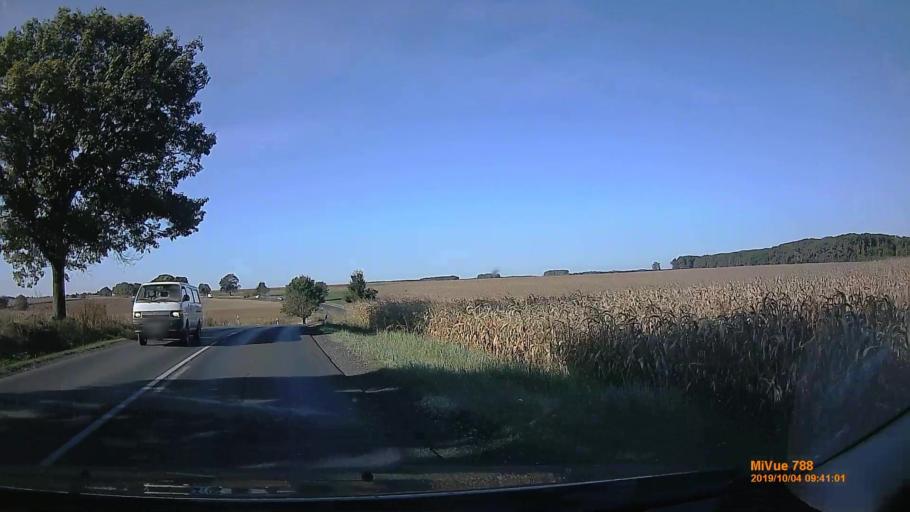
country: HU
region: Somogy
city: Kaposvar
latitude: 46.4356
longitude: 17.7897
